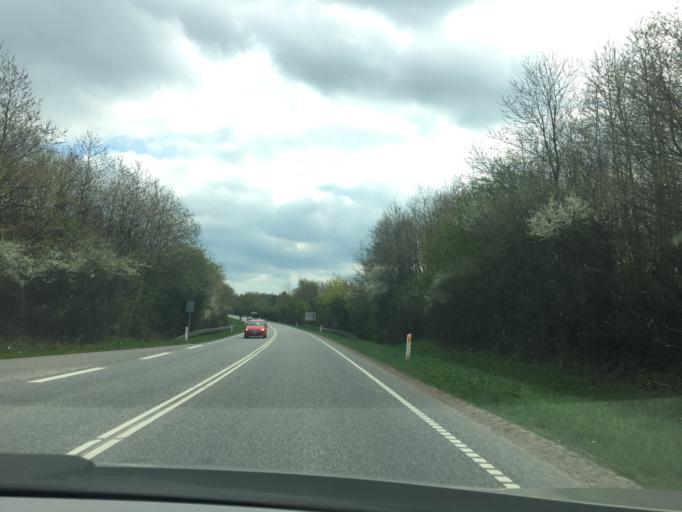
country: DK
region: Central Jutland
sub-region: Horsens Kommune
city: Braedstrup
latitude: 55.9690
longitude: 9.6022
